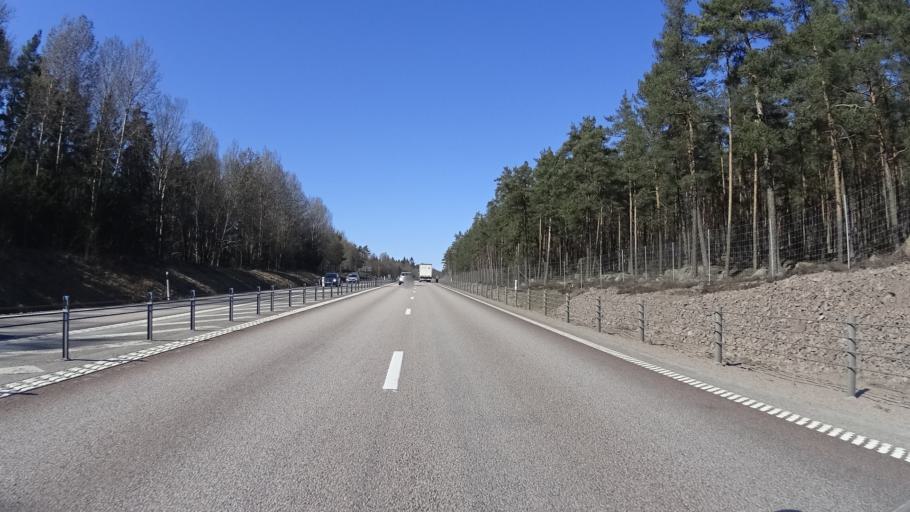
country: SE
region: Vaermland
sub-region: Kristinehamns Kommun
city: Kristinehamn
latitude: 59.3336
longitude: 14.0957
